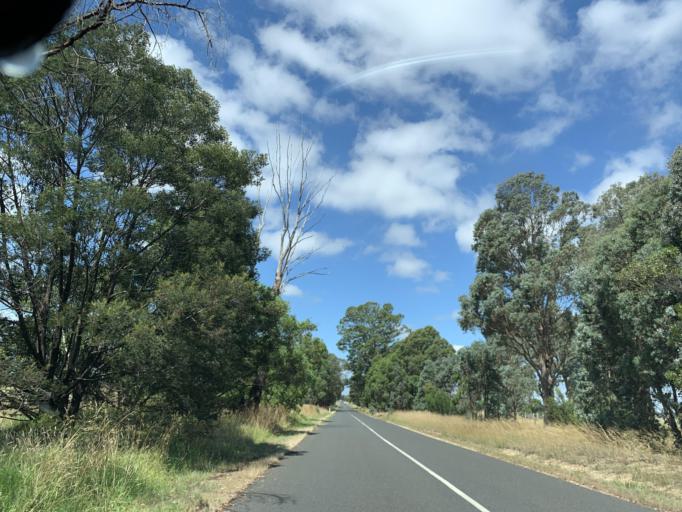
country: AU
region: Victoria
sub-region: Wellington
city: Heyfield
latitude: -38.0101
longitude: 146.6570
